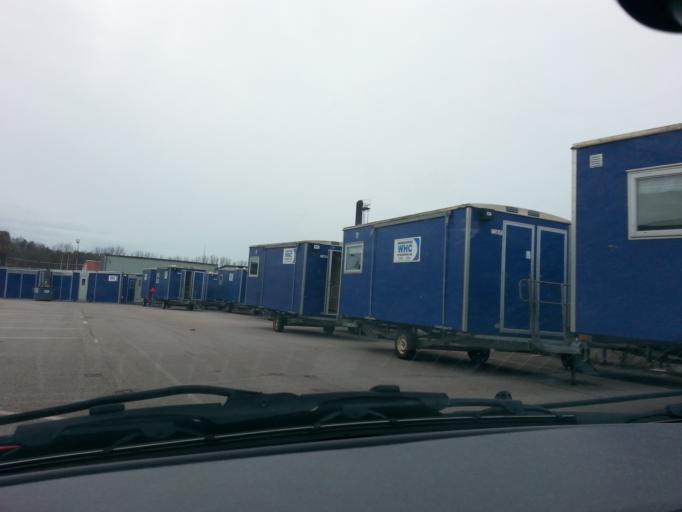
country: SE
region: Vaestra Goetaland
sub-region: Goteborg
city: Goeteborg
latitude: 57.7272
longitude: 11.9891
